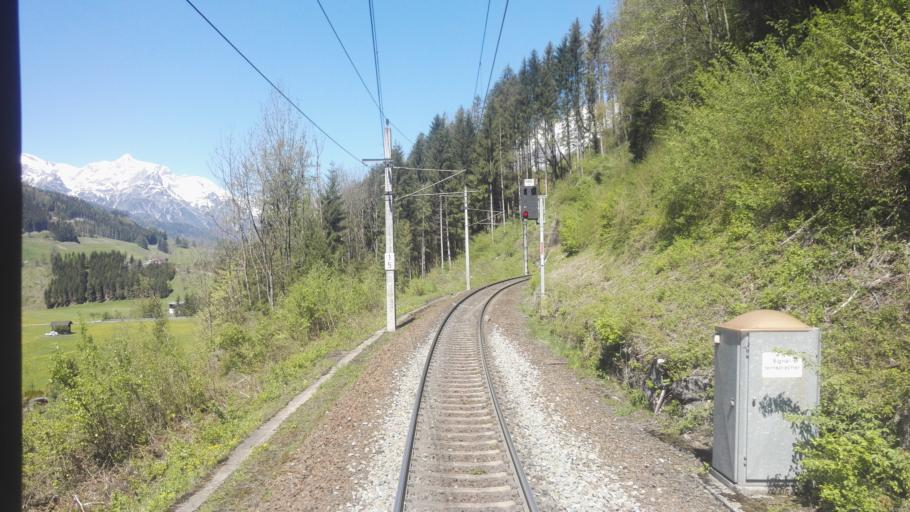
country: AT
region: Salzburg
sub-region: Politischer Bezirk Sankt Johann im Pongau
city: Bischofshofen
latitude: 47.4308
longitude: 13.2236
